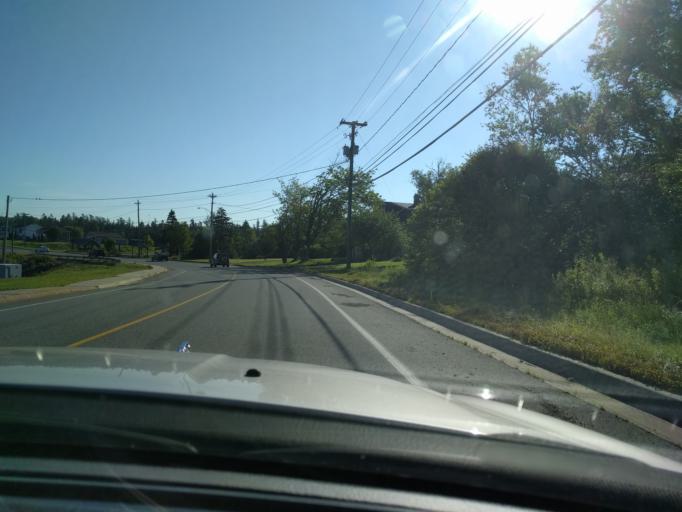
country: US
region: Maine
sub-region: Washington County
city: Eastport
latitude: 45.0617
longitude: -66.7822
